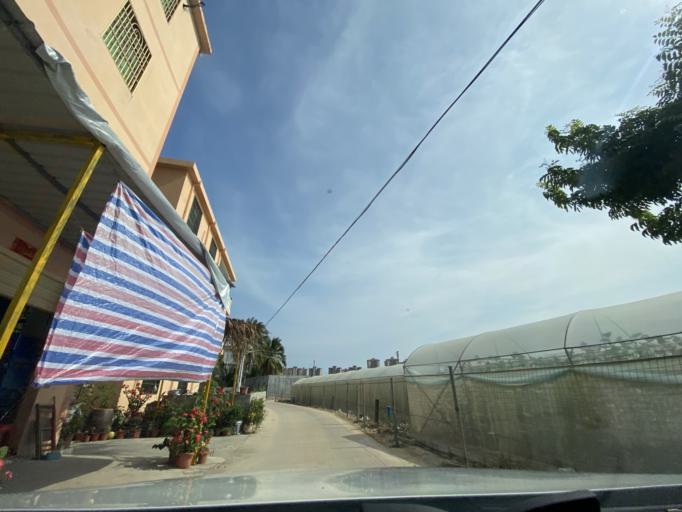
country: CN
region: Hainan
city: Yingzhou
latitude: 18.4068
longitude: 109.8311
